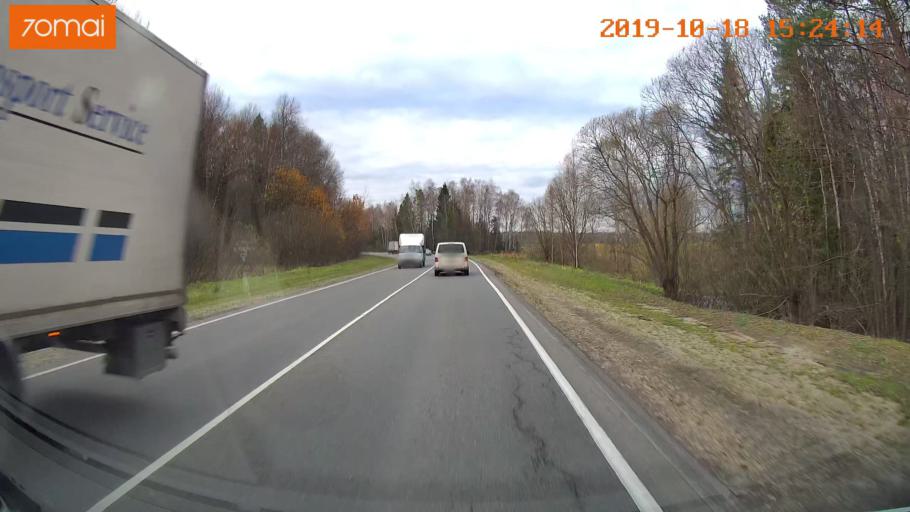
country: RU
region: Vladimir
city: Anopino
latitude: 55.7320
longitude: 40.7247
